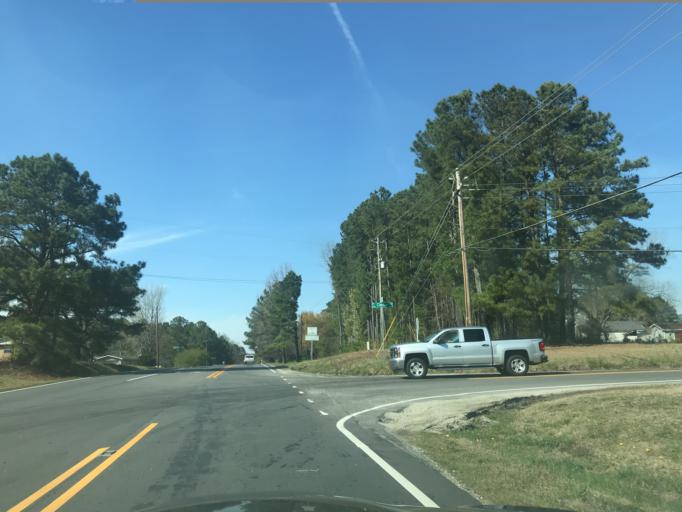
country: US
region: North Carolina
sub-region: Wake County
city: Fuquay-Varina
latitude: 35.5620
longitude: -78.7547
